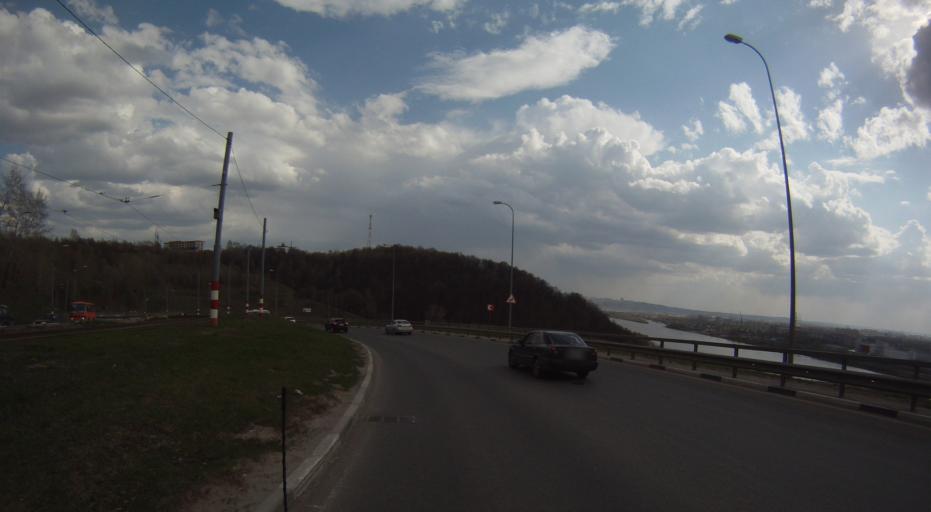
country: RU
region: Nizjnij Novgorod
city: Nizhniy Novgorod
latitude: 56.3012
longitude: 43.9702
